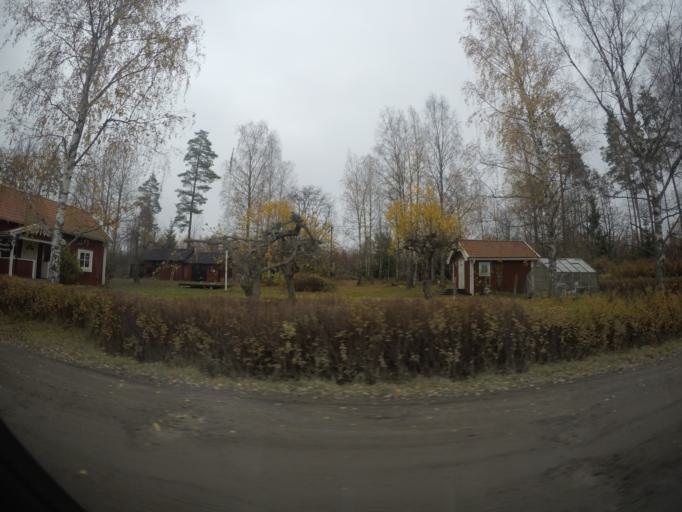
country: SE
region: Vaestmanland
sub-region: Surahammars Kommun
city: Ramnas
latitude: 59.7059
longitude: 16.0915
